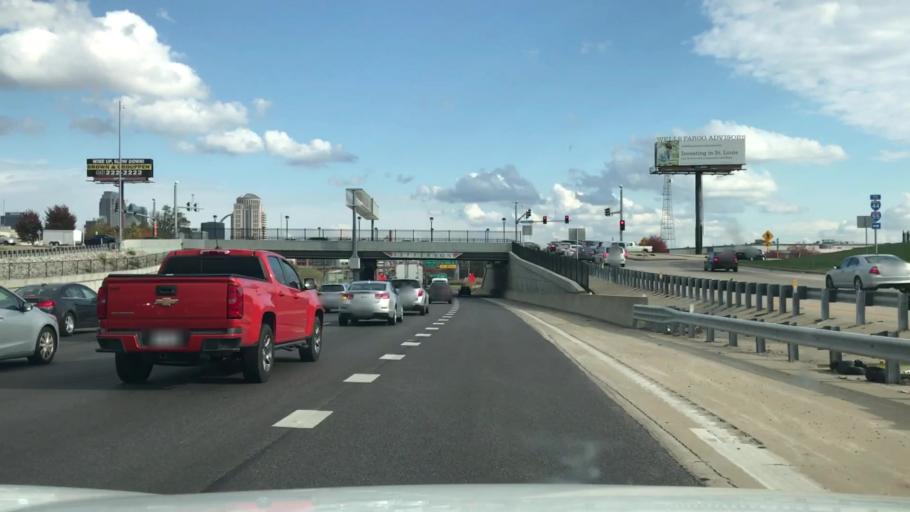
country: US
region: Missouri
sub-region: City of Saint Louis
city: St. Louis
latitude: 38.6278
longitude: -90.2192
